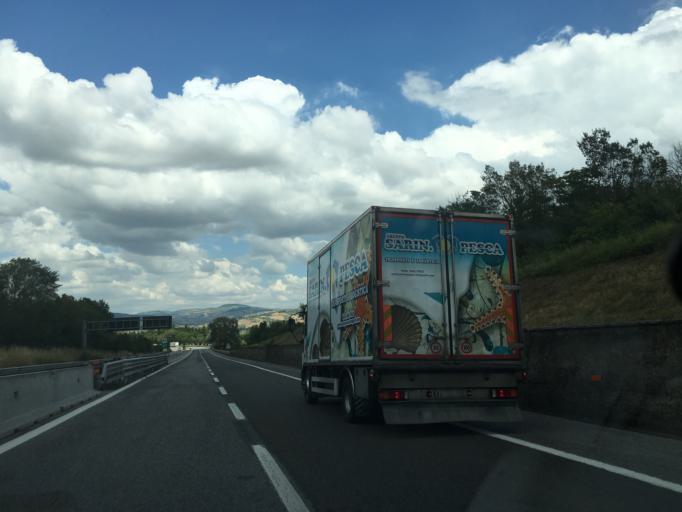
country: IT
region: Campania
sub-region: Provincia di Avellino
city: Grottaminarda
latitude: 41.0650
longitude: 15.0664
